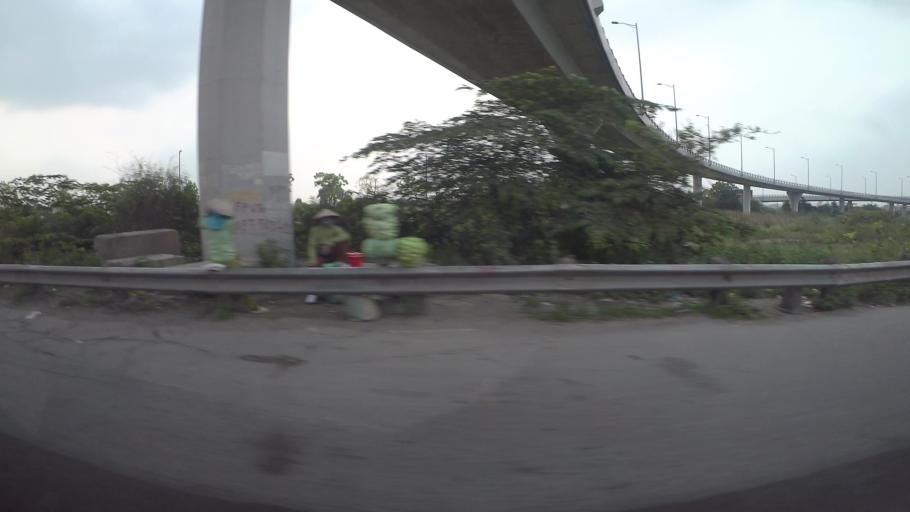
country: VN
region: Ha Noi
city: Trau Quy
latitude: 21.0111
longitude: 105.9169
